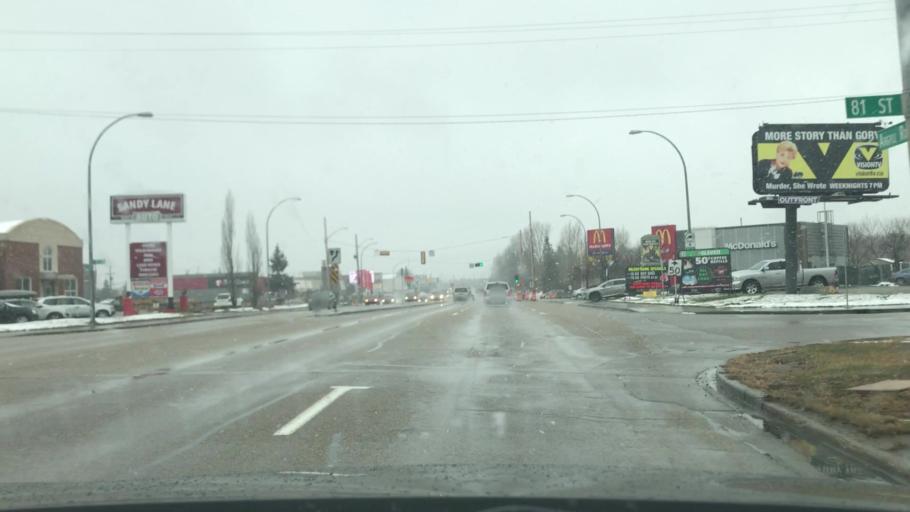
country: CA
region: Alberta
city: Edmonton
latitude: 53.5040
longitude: -113.4514
